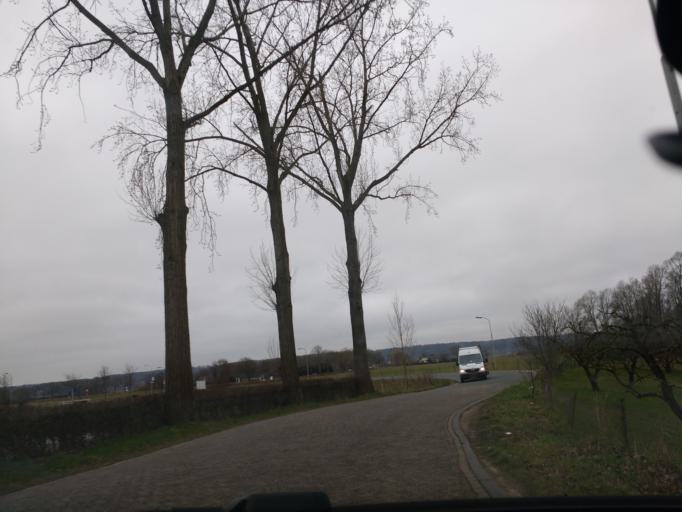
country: NL
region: Gelderland
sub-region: Gemeente Groesbeek
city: Berg en Dal
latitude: 51.8520
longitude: 5.9391
